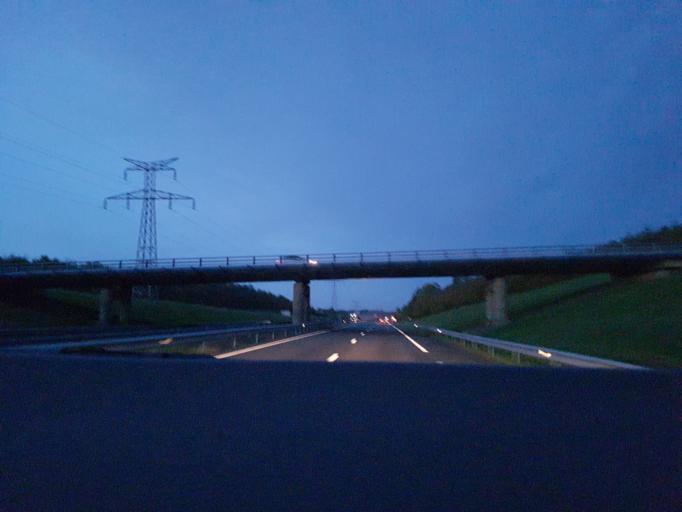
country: FR
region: Pays de la Loire
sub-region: Departement de la Mayenne
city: Louverne
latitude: 48.1296
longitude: -0.7165
